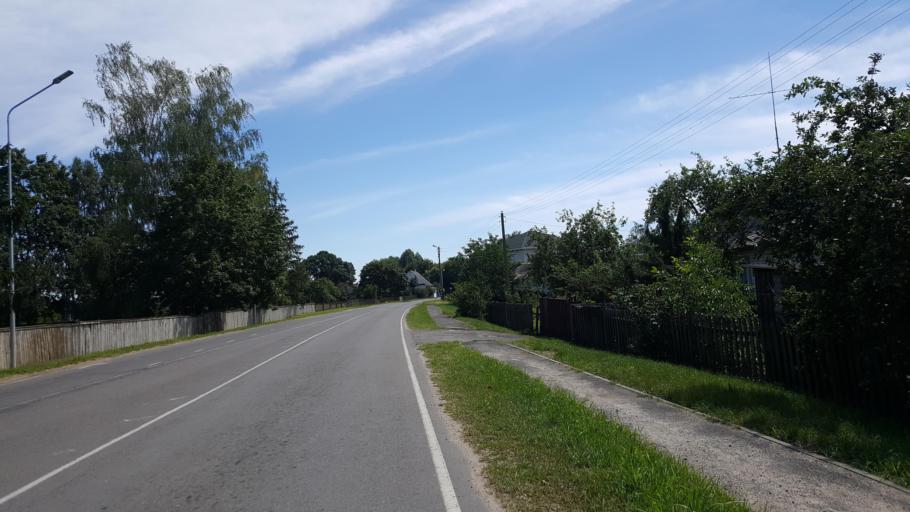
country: BY
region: Brest
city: Pruzhany
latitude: 52.5659
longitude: 24.2129
